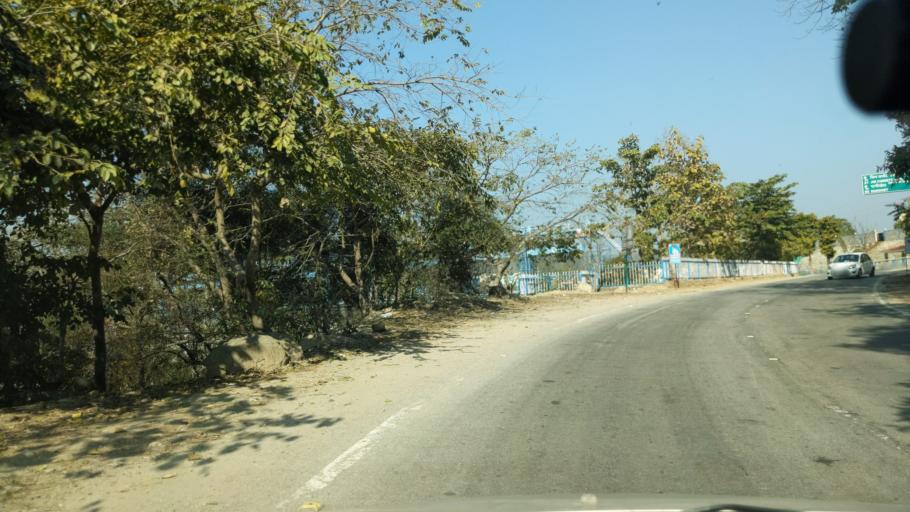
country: IN
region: Uttarakhand
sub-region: Naini Tal
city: Ramnagar
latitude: 29.3981
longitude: 79.1351
